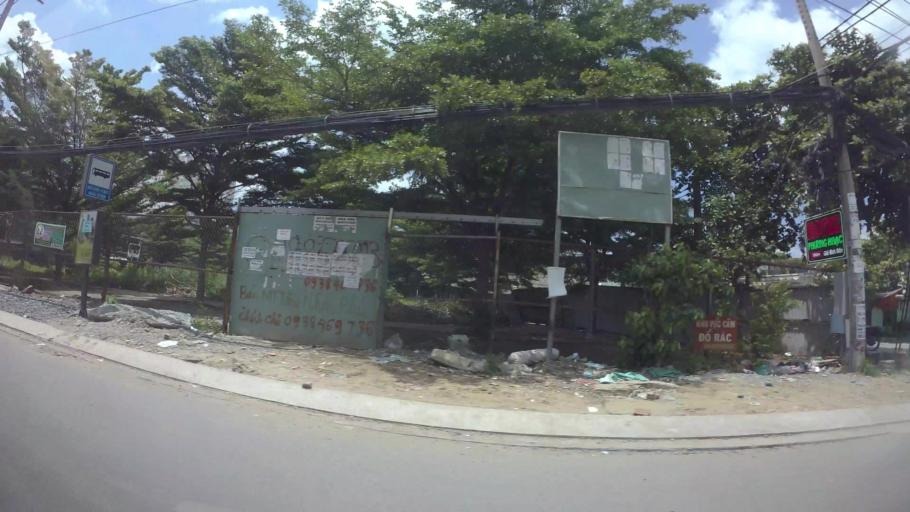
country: VN
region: Ho Chi Minh City
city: Quan Chin
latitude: 10.8275
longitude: 106.7713
